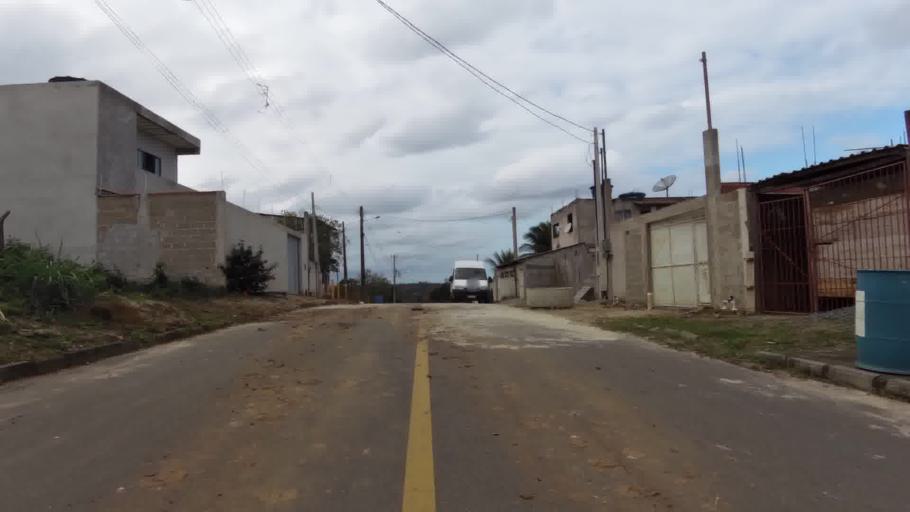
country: BR
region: Espirito Santo
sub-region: Piuma
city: Piuma
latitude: -20.7953
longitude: -40.6417
